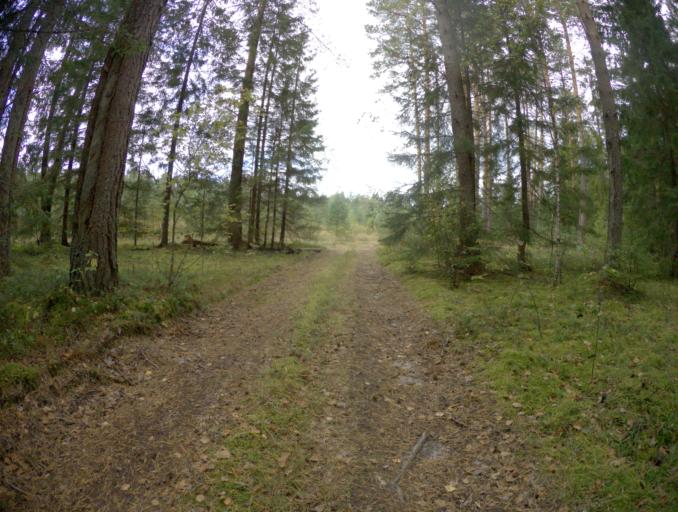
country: RU
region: Vladimir
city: Golovino
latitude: 55.9036
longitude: 40.4427
